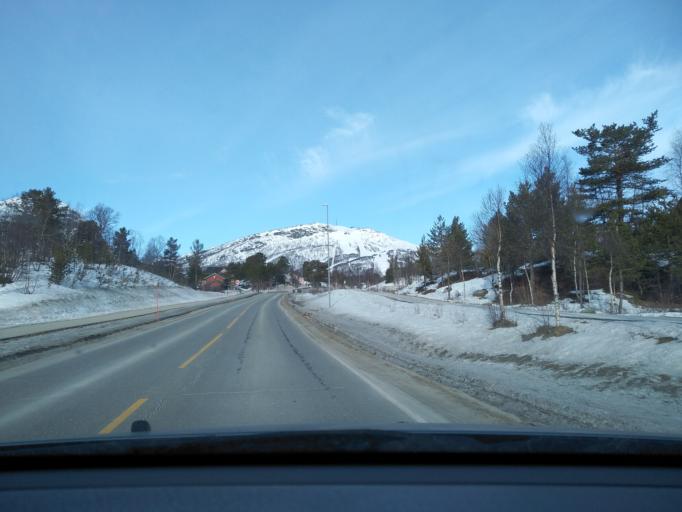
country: NO
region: Aust-Agder
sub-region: Bykle
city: Hovden
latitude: 59.5566
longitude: 7.3601
